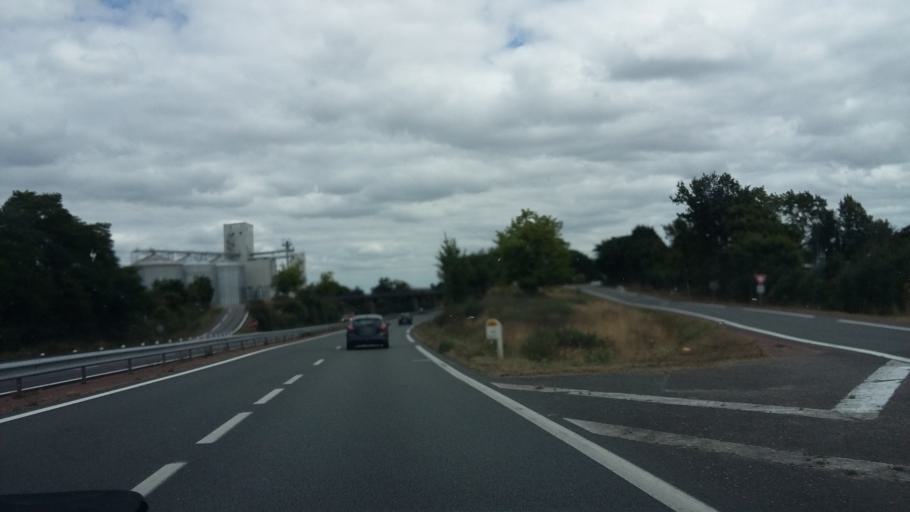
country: FR
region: Pays de la Loire
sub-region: Departement de la Vendee
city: La Genetouze
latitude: 46.7096
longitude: -1.5214
